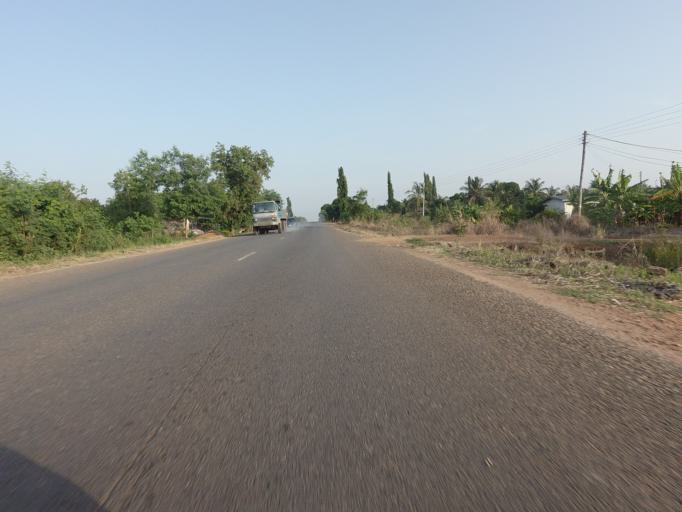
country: GH
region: Volta
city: Anloga
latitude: 6.0158
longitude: 0.6662
